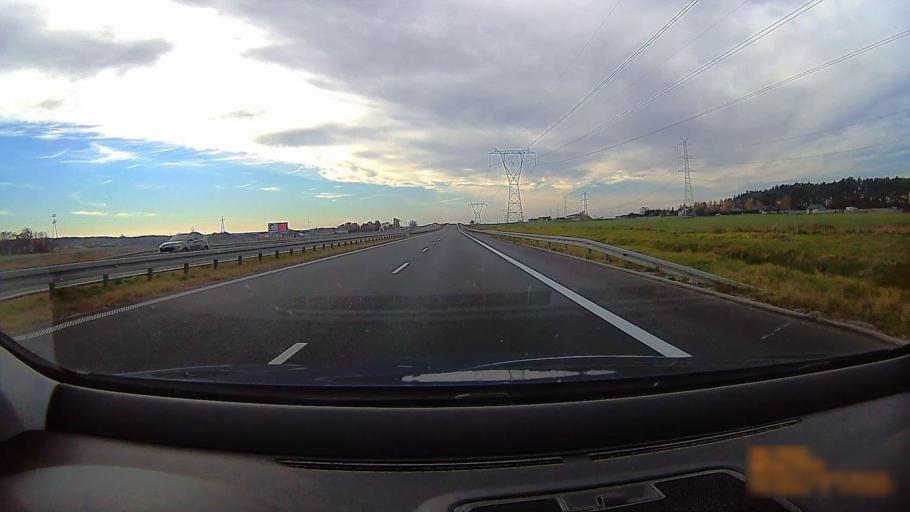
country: PL
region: Greater Poland Voivodeship
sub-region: Powiat ostrowski
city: Przygodzice
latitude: 51.6106
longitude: 17.8569
